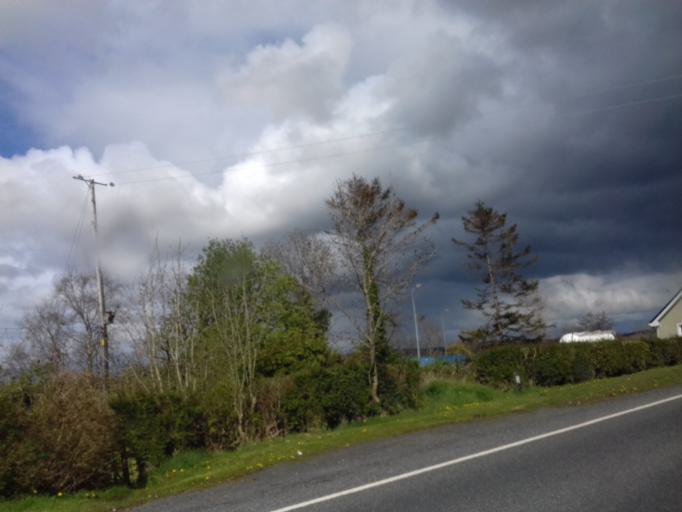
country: IE
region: Ulster
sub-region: County Donegal
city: Ballyshannon
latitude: 54.4683
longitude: -8.0227
